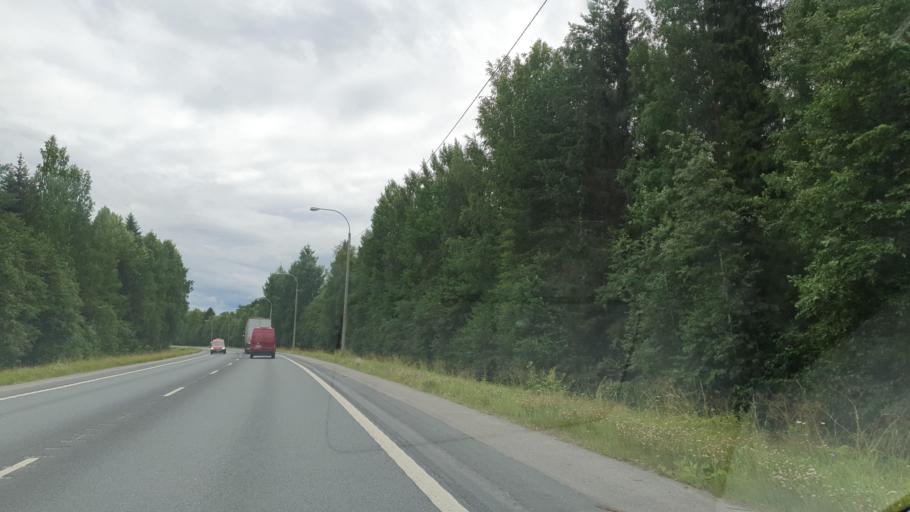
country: FI
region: Northern Savo
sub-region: Ylae-Savo
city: Iisalmi
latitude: 63.5086
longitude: 27.2571
